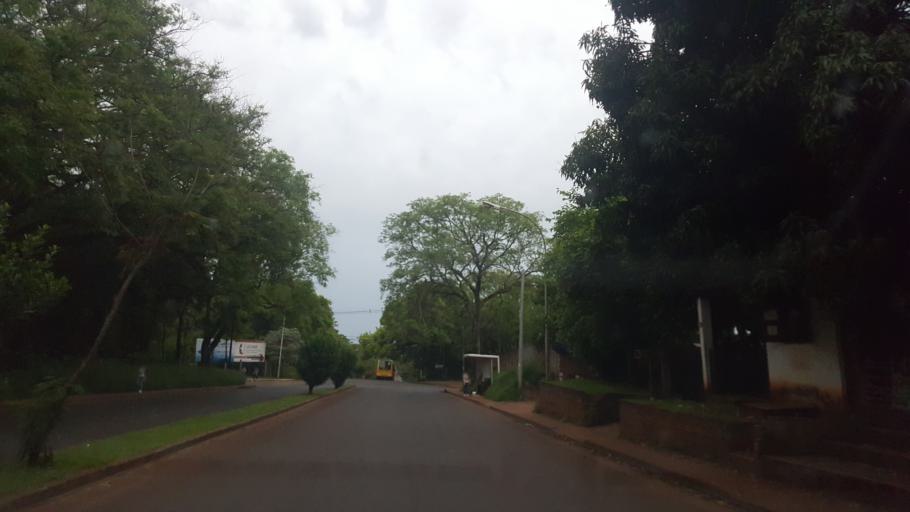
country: AR
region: Misiones
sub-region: Departamento de Capital
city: Posadas
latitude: -27.3572
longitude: -55.9379
